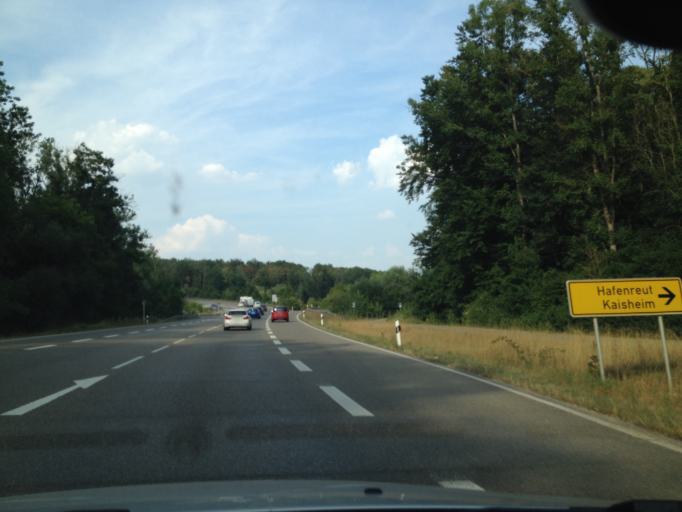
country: DE
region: Bavaria
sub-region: Swabia
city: Kaisheim
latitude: 48.7569
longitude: 10.7773
